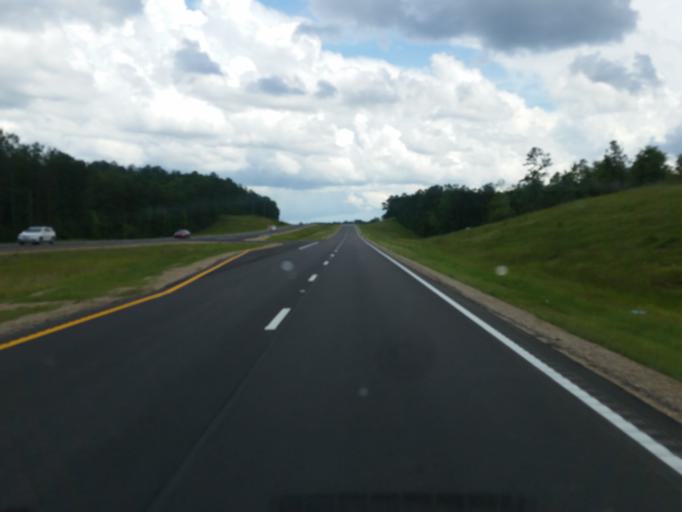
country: US
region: Mississippi
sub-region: George County
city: Lucedale
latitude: 31.0604
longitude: -88.7343
